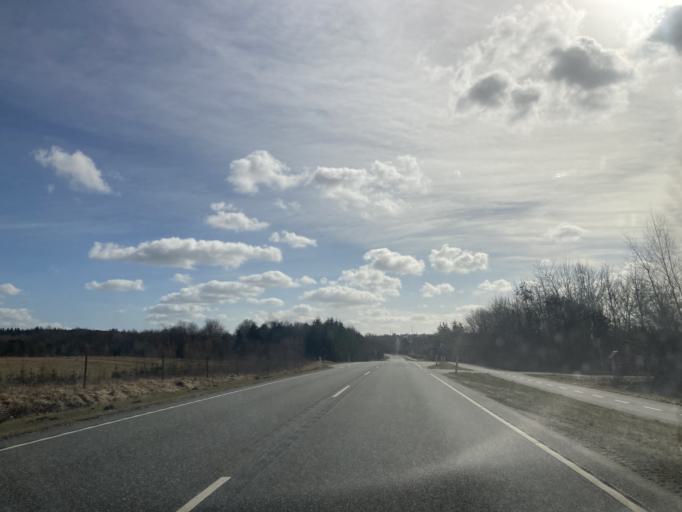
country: DK
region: Central Jutland
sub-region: Hedensted Kommune
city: Torring
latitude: 55.9831
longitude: 9.3929
